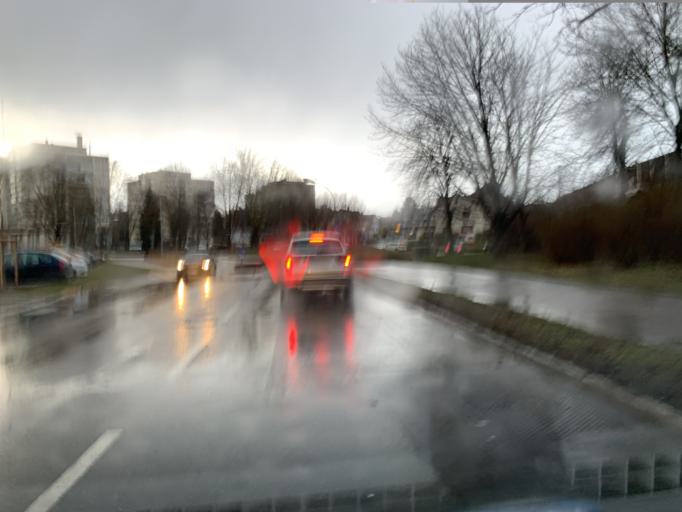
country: DE
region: Baden-Wuerttemberg
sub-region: Regierungsbezirk Stuttgart
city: Magstadt
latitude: 48.7180
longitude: 8.9703
